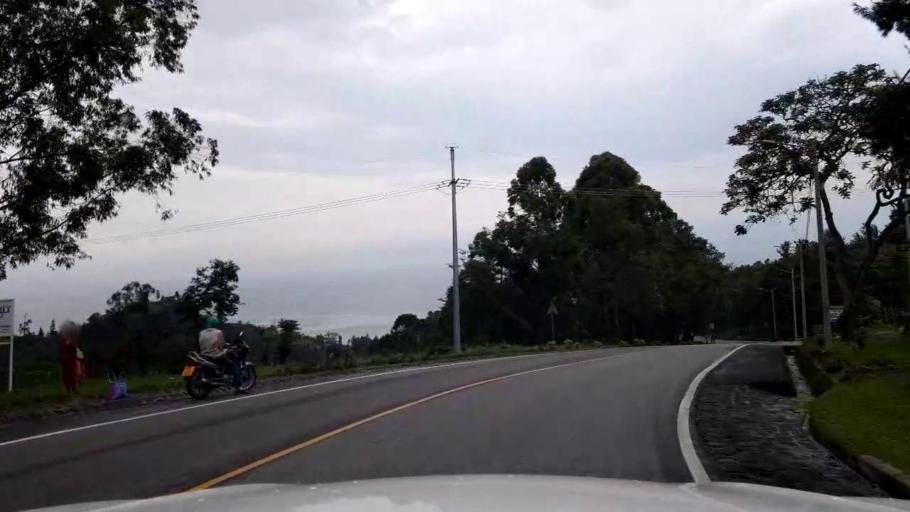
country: RW
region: Western Province
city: Gisenyi
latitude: -1.7041
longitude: 29.2702
